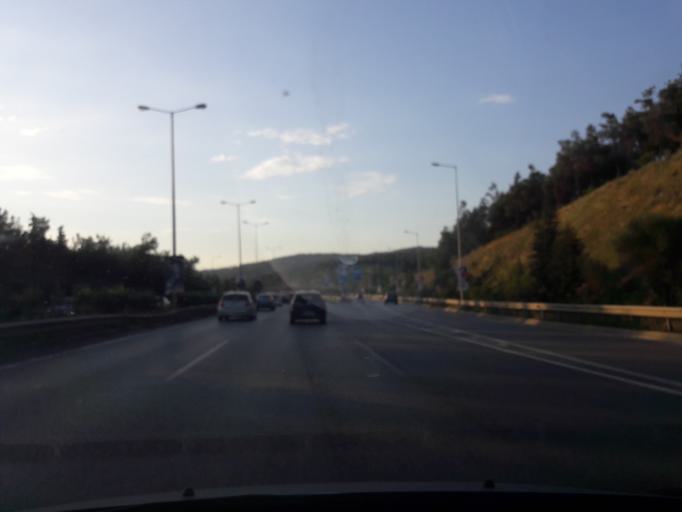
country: GR
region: Central Macedonia
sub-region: Nomos Thessalonikis
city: Triandria
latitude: 40.6186
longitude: 22.9833
